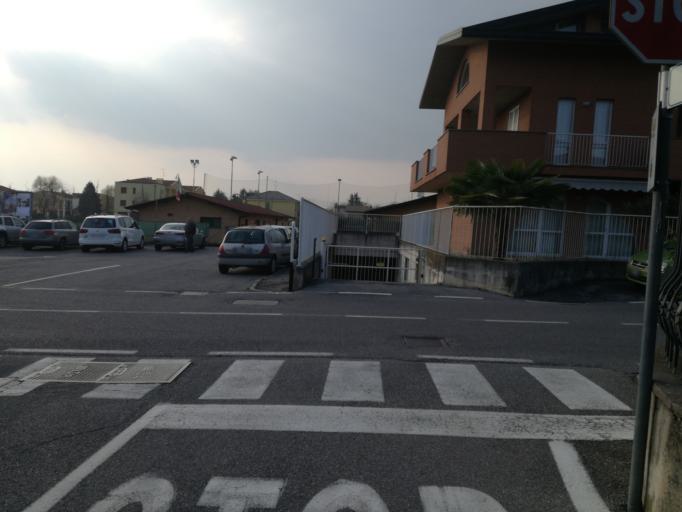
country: IT
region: Lombardy
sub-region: Provincia di Lecco
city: Verderio Inferiore
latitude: 45.6642
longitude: 9.4342
